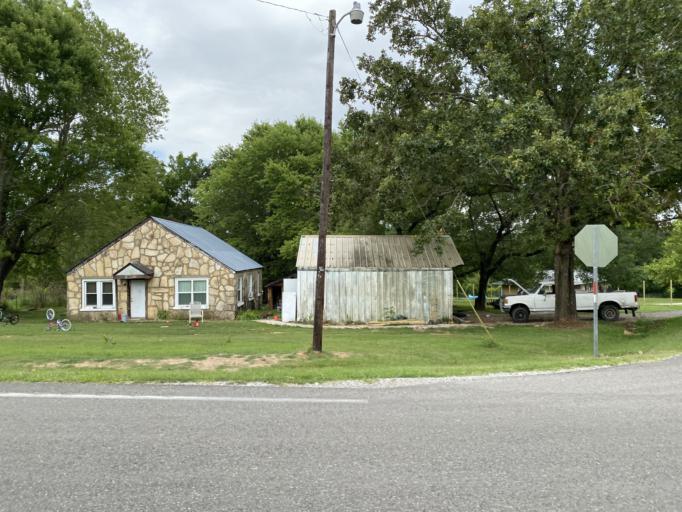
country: US
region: Arkansas
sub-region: Fulton County
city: Salem
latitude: 36.3616
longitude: -91.8318
